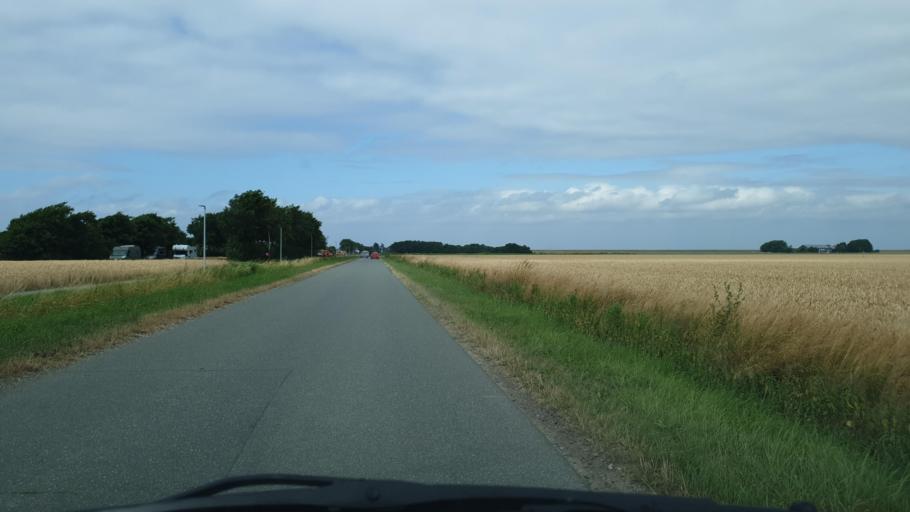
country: DE
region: Schleswig-Holstein
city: Friedrichskoog
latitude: 54.0309
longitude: 8.8472
